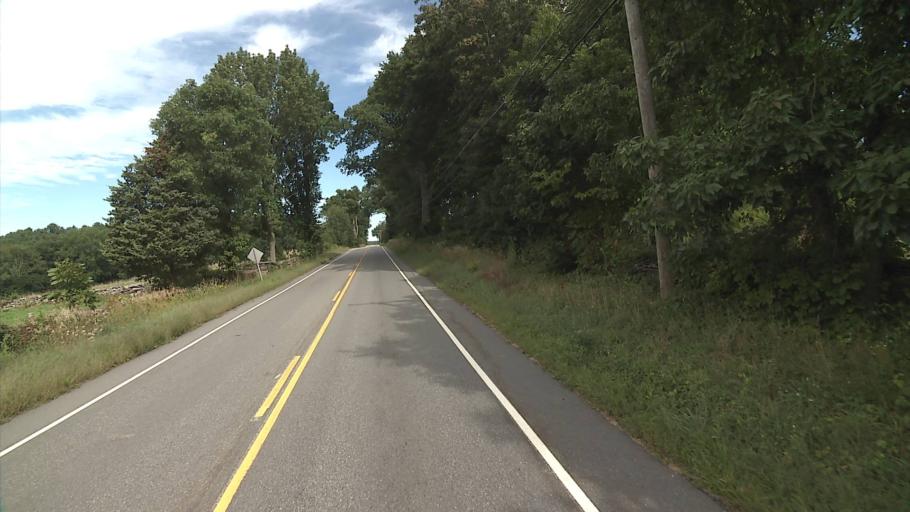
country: US
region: Connecticut
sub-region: Tolland County
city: South Coventry
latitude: 41.8093
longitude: -72.3059
